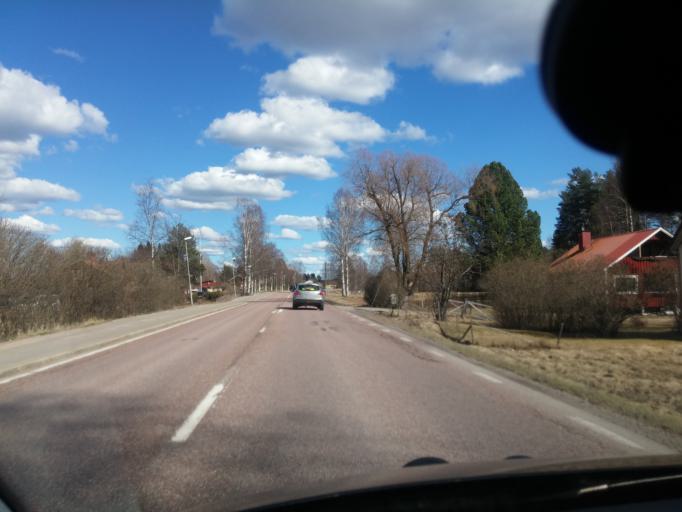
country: SE
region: Gaevleborg
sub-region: Ljusdals Kommun
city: Farila
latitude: 61.8012
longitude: 15.8739
